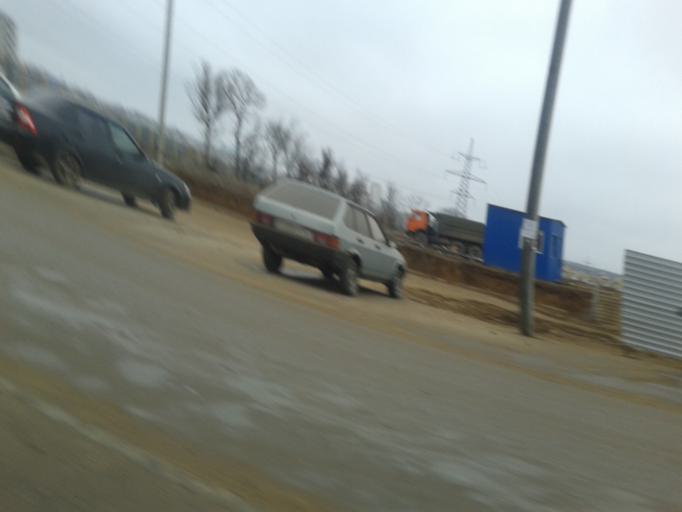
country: RU
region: Volgograd
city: Volgograd
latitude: 48.6623
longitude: 44.4140
